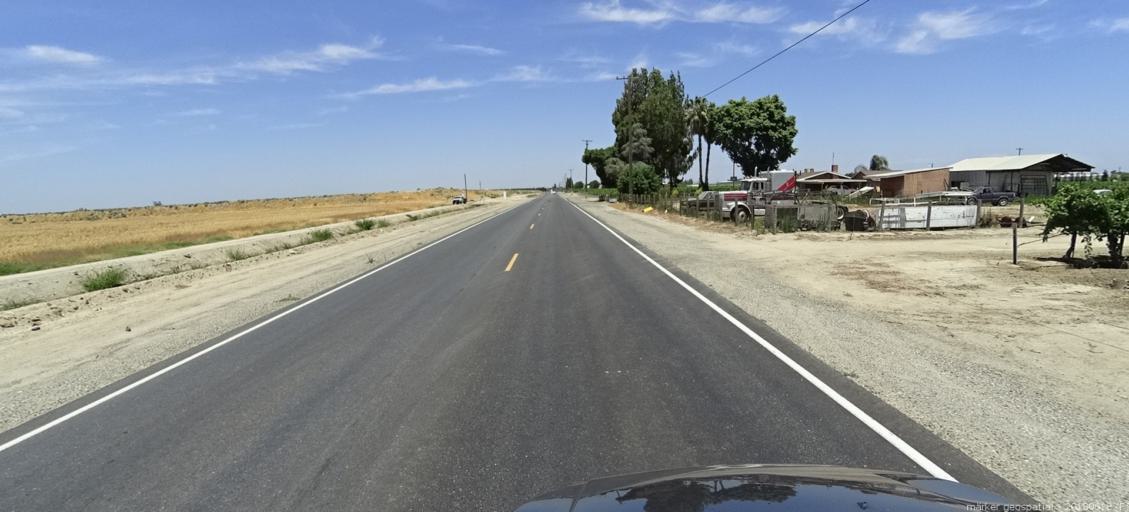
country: US
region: California
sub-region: Madera County
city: Madera
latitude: 36.9281
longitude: -120.0923
